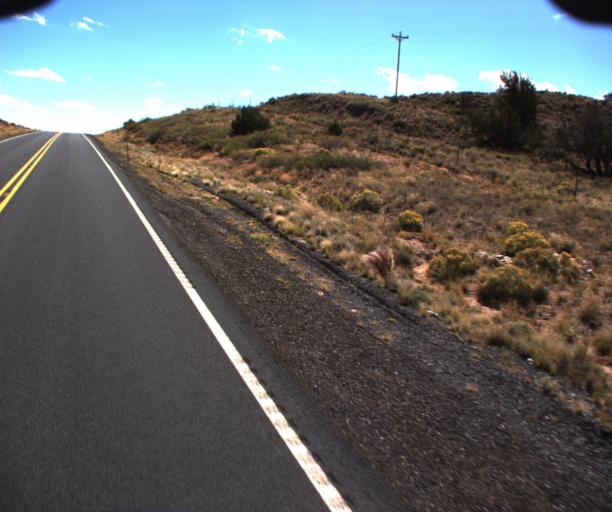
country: US
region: Arizona
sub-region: Apache County
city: Houck
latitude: 35.0343
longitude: -109.2614
